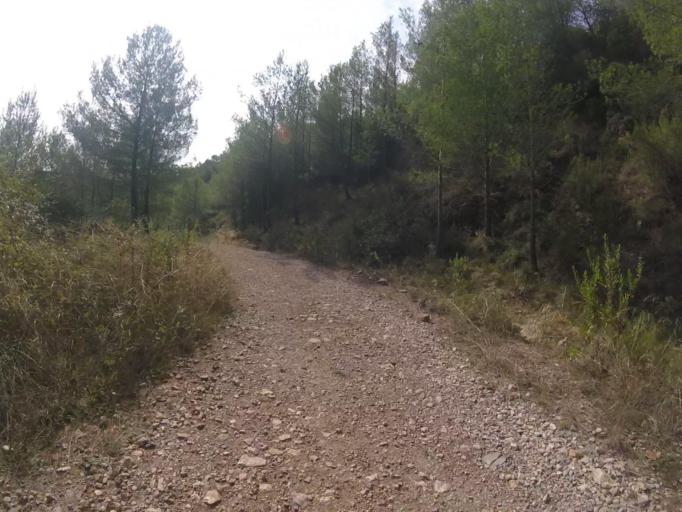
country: ES
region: Valencia
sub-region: Provincia de Castello
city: Benicassim
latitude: 40.0856
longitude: 0.0483
